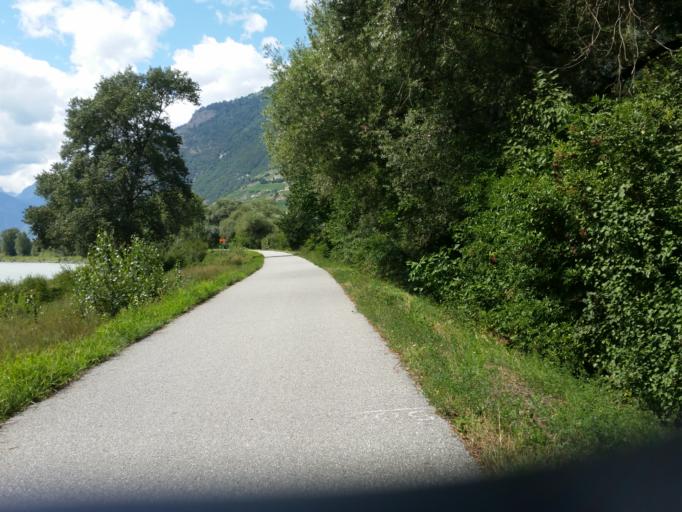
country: CH
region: Valais
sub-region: Martigny District
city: Leytron
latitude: 46.1783
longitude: 7.2092
